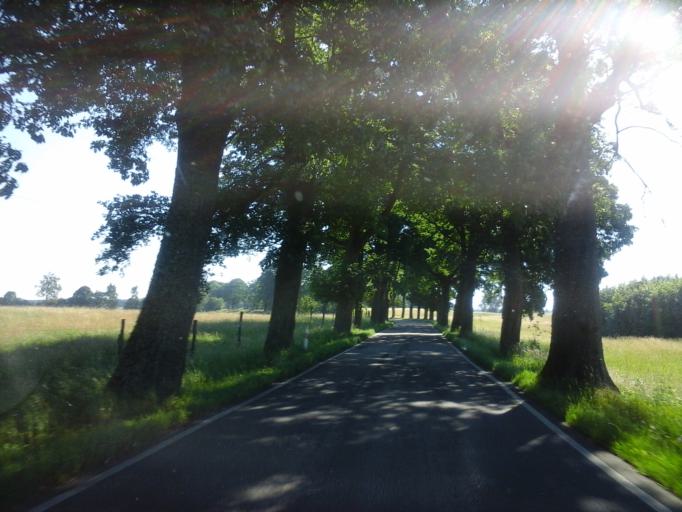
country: PL
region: West Pomeranian Voivodeship
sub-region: Powiat drawski
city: Drawsko Pomorskie
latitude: 53.5762
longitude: 15.8729
